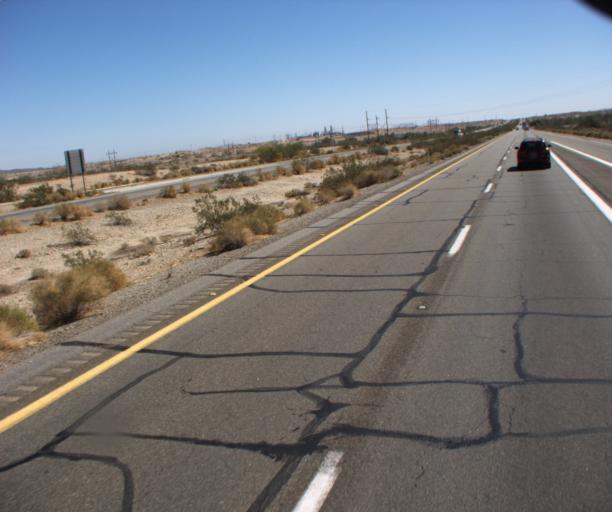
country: US
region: Arizona
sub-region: Yuma County
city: Fortuna Foothills
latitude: 32.6660
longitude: -114.2799
